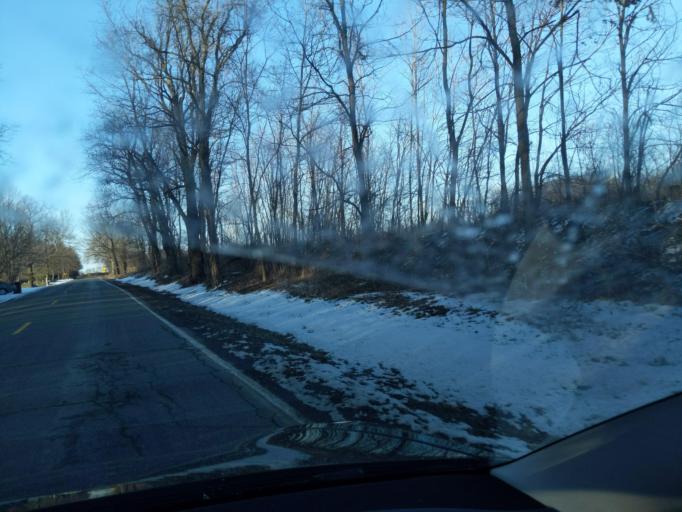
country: US
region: Michigan
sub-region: Ingham County
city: Stockbridge
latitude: 42.5316
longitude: -84.2781
